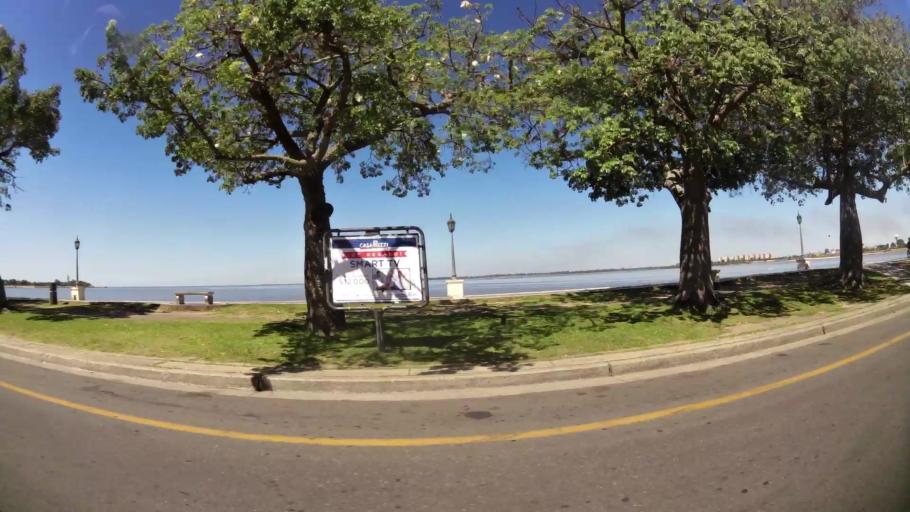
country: AR
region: Santa Fe
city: Santa Fe de la Vera Cruz
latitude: -31.6284
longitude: -60.6782
